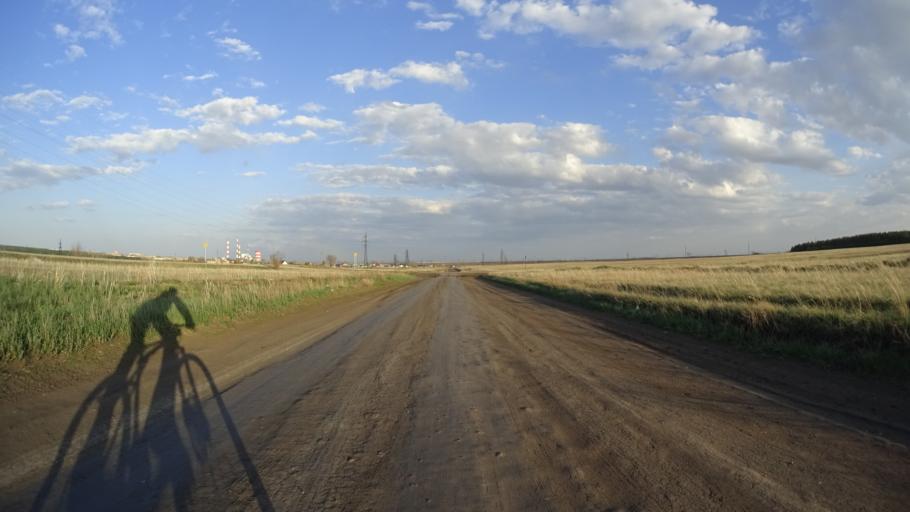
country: RU
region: Chelyabinsk
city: Troitsk
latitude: 54.0503
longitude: 61.5943
